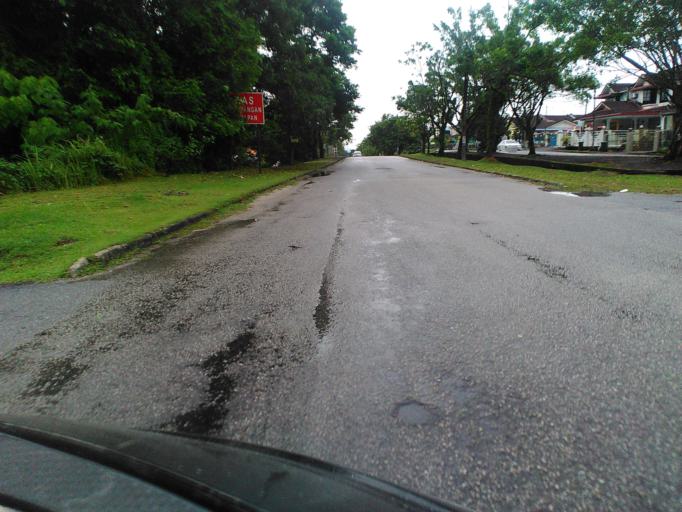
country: MY
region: Kedah
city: Kulim
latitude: 5.3677
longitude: 100.5660
